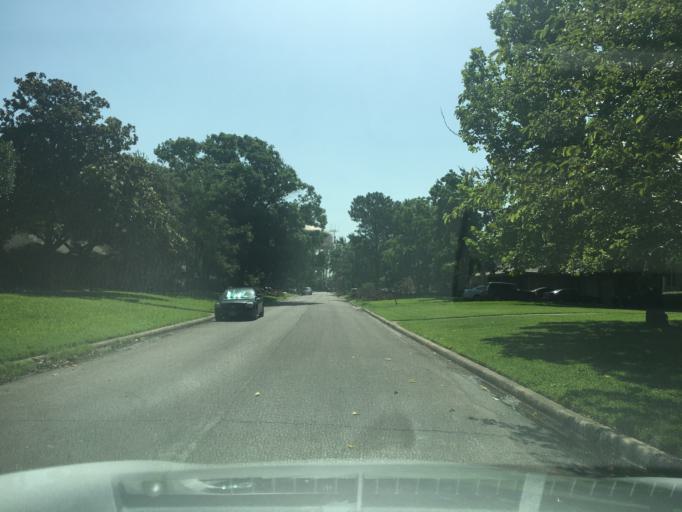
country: US
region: Texas
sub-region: Dallas County
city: Addison
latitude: 32.9085
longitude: -96.8105
